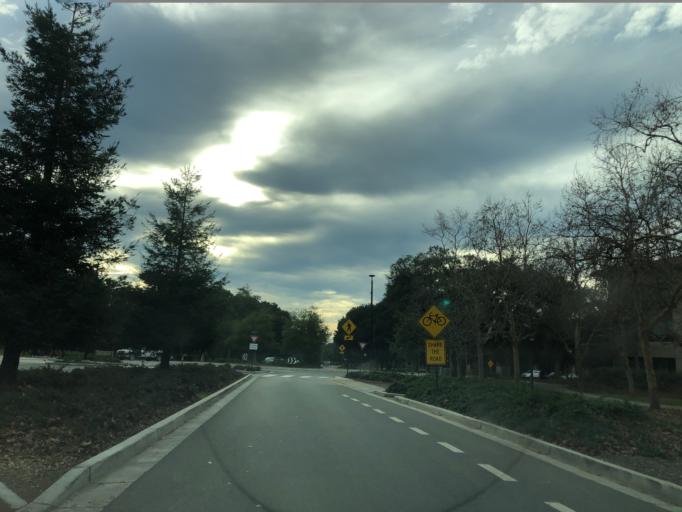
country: US
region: California
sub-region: Santa Clara County
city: Stanford
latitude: 37.4319
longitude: -122.1640
